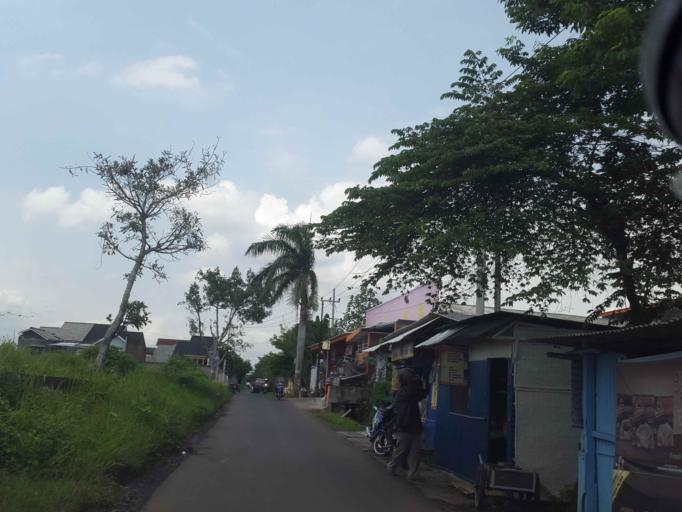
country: ID
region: East Java
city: Singosari
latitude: -7.9079
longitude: 112.6500
